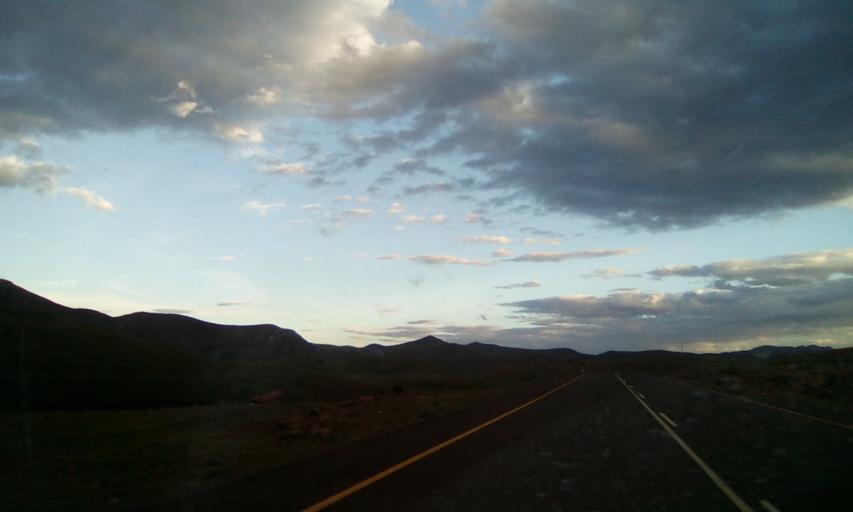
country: LS
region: Maseru
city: Nako
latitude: -29.8091
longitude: 28.0303
